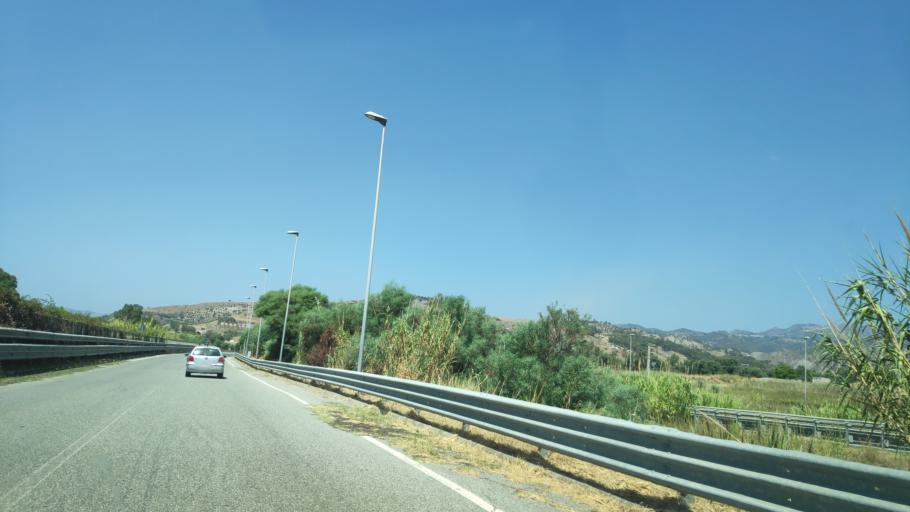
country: IT
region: Calabria
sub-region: Provincia di Reggio Calabria
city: Palizzi Marina
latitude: 37.9216
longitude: 15.9571
